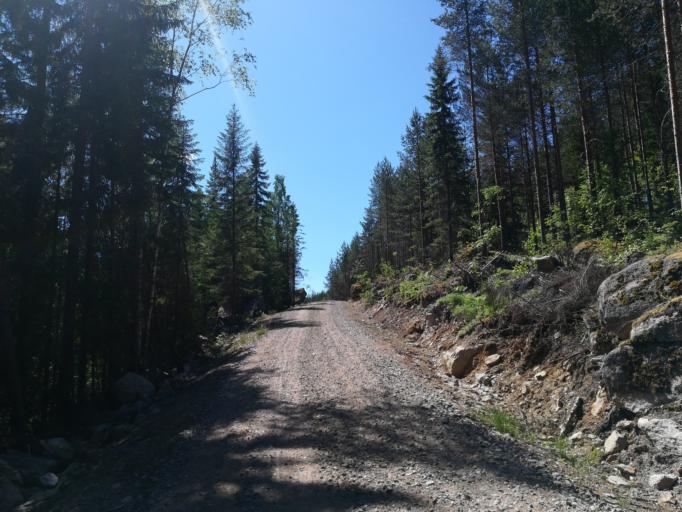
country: FI
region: Southern Savonia
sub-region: Mikkeli
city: Puumala
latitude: 61.6172
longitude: 28.1716
